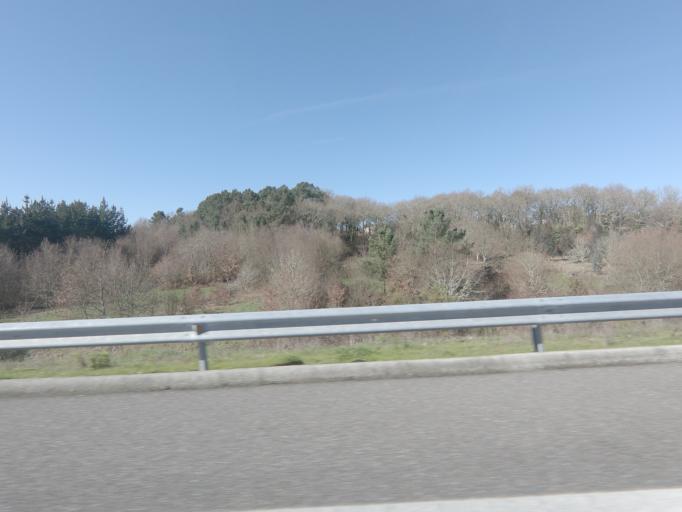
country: ES
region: Galicia
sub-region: Provincia de Ourense
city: Maside
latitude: 42.4259
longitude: -8.0131
